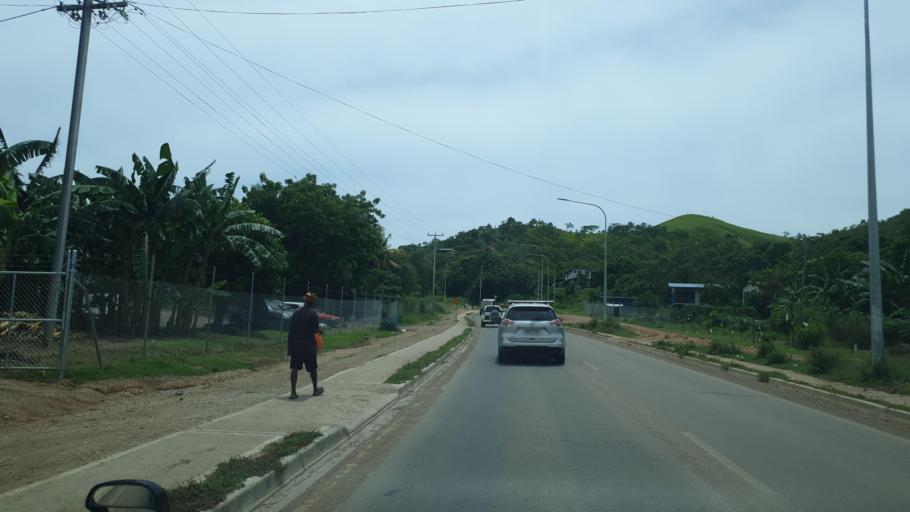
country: PG
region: National Capital
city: Port Moresby
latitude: -9.5150
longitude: 147.2406
